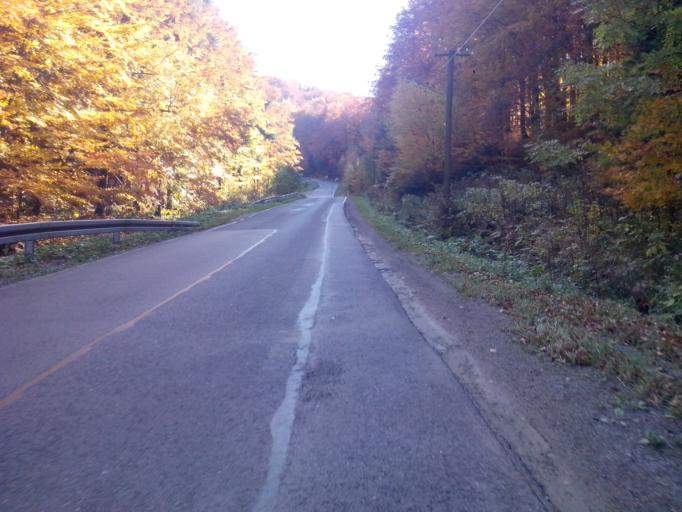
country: PL
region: Subcarpathian Voivodeship
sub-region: Powiat krosnienski
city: Korczyna
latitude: 49.7582
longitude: 21.7938
